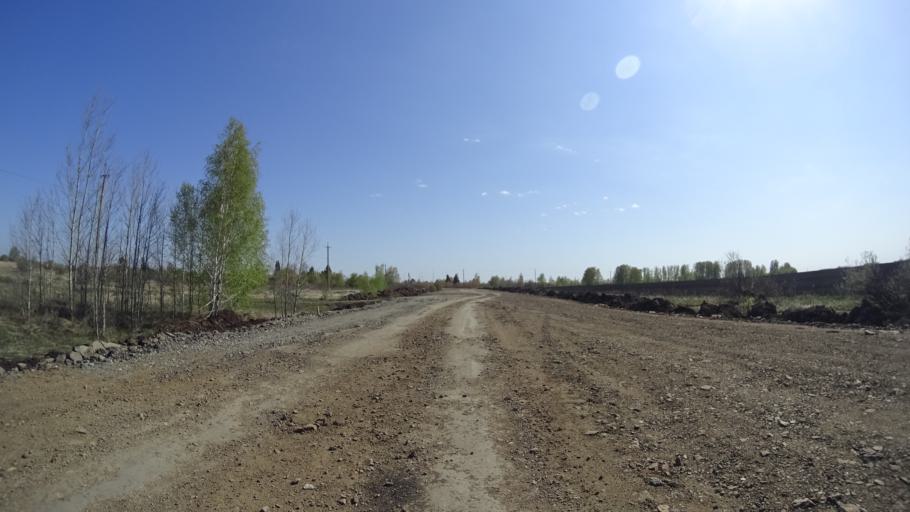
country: RU
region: Chelyabinsk
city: Troitsk
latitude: 54.1852
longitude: 61.4967
